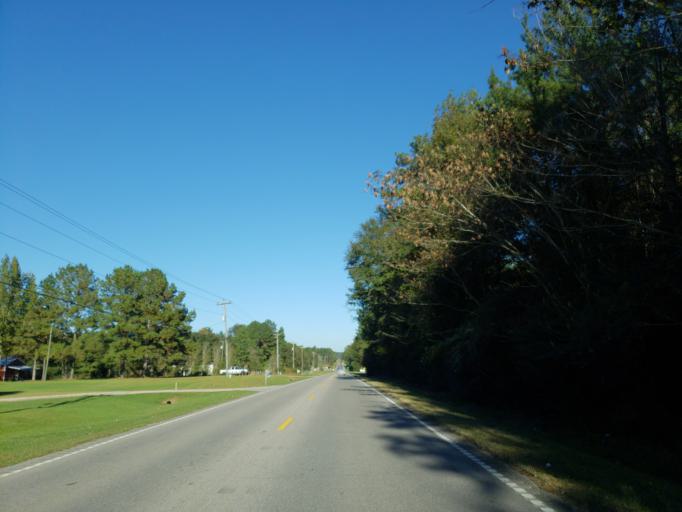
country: US
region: Mississippi
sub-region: Forrest County
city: Petal
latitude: 31.3619
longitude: -89.1493
